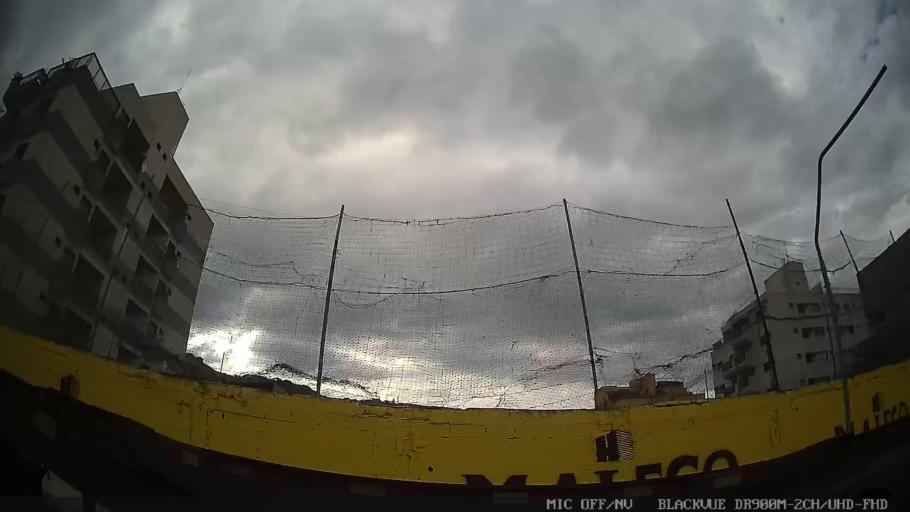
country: BR
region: Sao Paulo
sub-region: Guaruja
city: Guaruja
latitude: -23.9816
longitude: -46.2342
